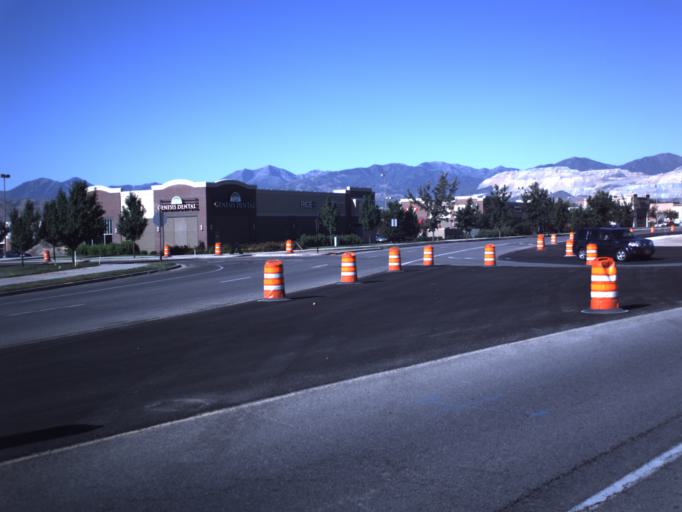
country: US
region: Utah
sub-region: Salt Lake County
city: South Jordan Heights
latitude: 40.5443
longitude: -111.9791
